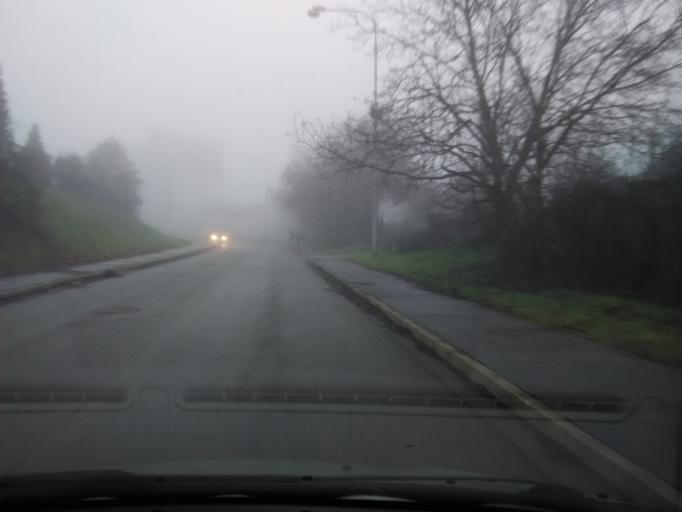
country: SK
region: Nitriansky
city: Levice
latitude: 48.2122
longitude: 18.6241
